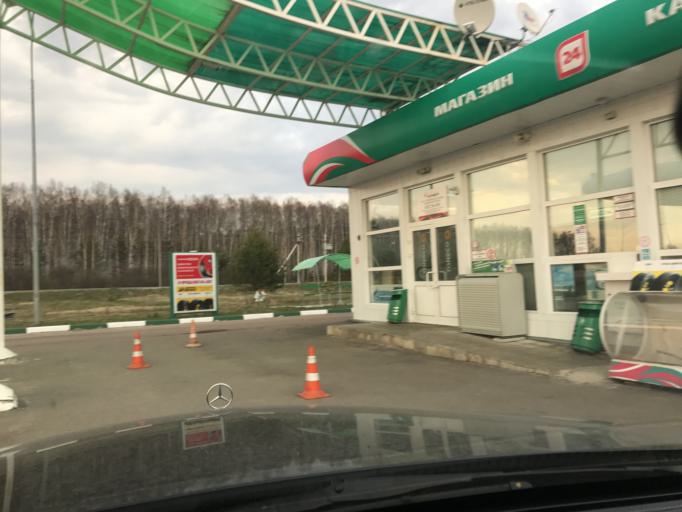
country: RU
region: Vladimir
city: Murom
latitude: 55.6228
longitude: 41.9009
